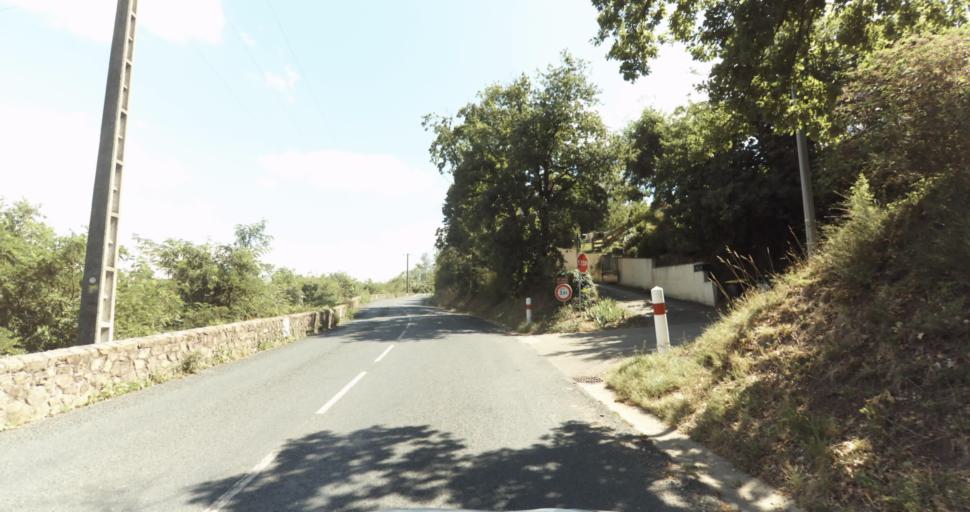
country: FR
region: Rhone-Alpes
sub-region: Departement du Rhone
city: Francheville
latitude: 45.7245
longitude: 4.7721
